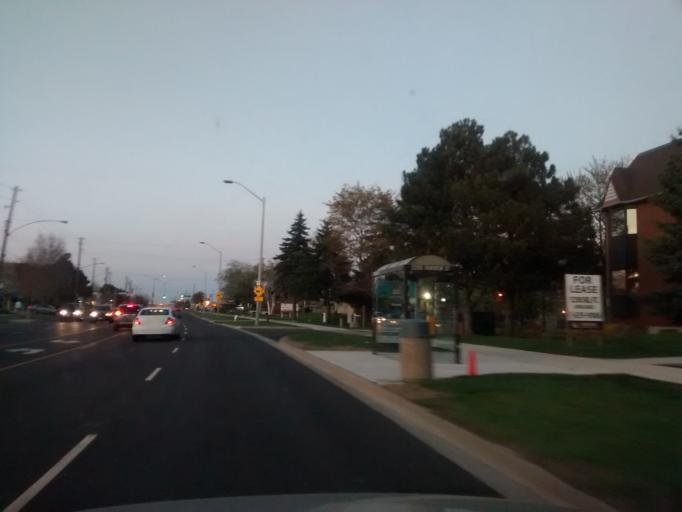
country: CA
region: Ontario
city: Burlington
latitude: 43.3412
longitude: -79.8054
